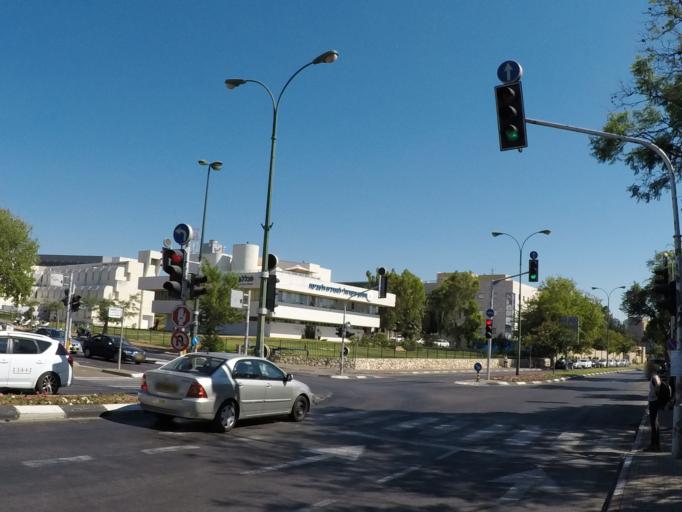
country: IL
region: Tel Aviv
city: Ramat Gan
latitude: 32.1066
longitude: 34.8006
